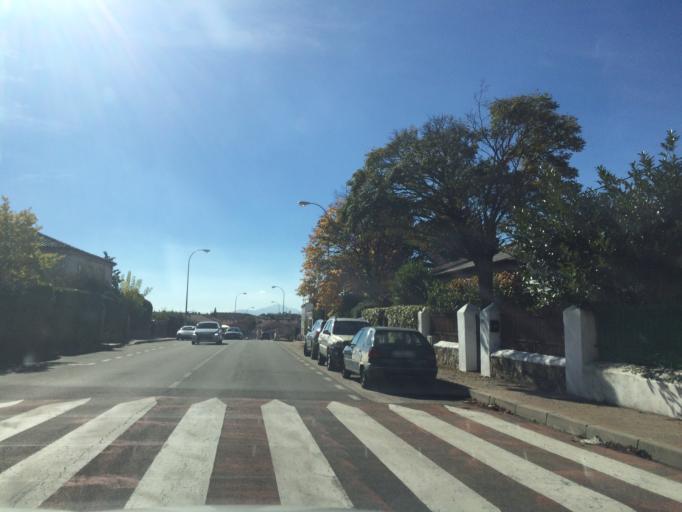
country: ES
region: Madrid
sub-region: Provincia de Madrid
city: La Cabrera
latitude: 40.8673
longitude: -3.6113
